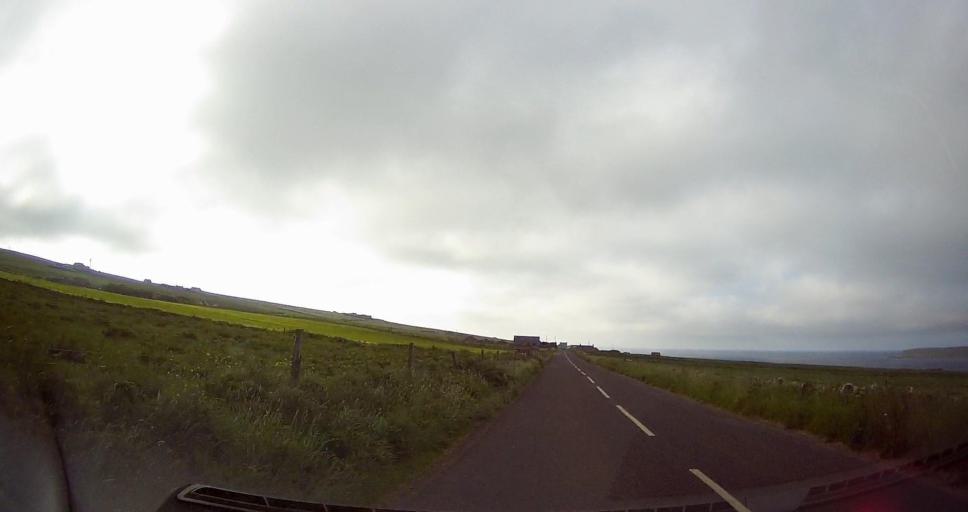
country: GB
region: Scotland
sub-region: Orkney Islands
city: Orkney
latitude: 59.1200
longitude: -3.1219
